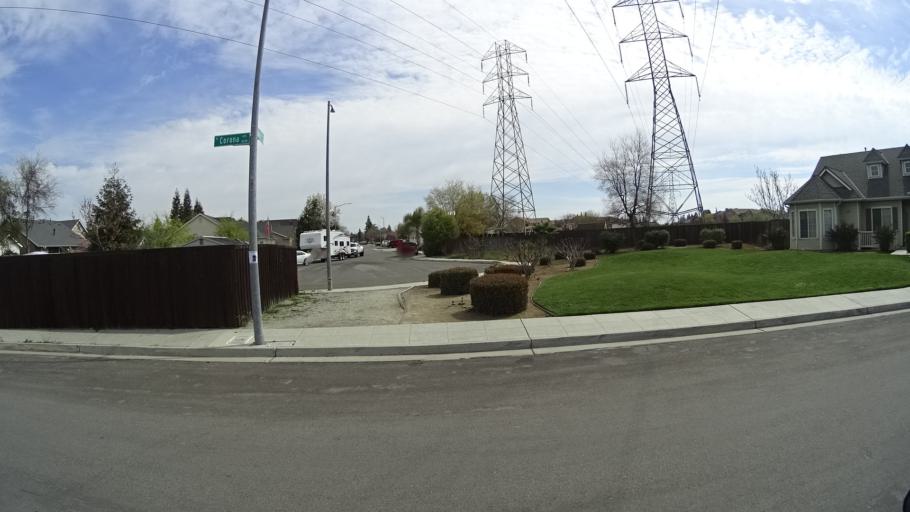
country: US
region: California
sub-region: Fresno County
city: West Park
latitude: 36.8195
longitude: -119.8778
